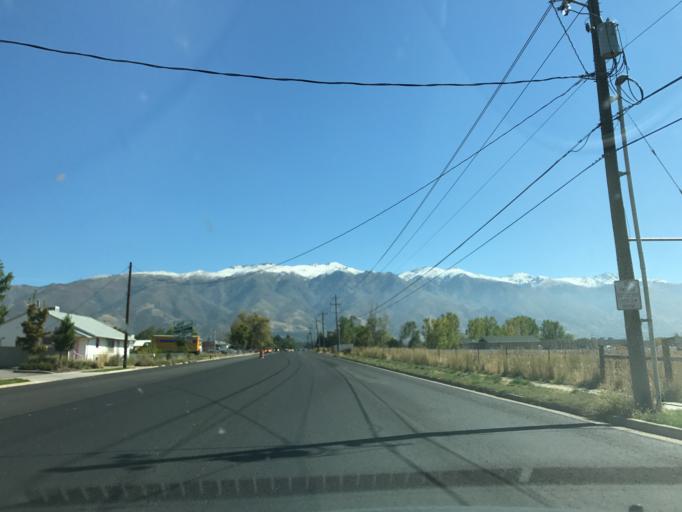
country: US
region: Utah
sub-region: Davis County
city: Hill Air Force Bace
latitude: 41.0891
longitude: -111.9644
